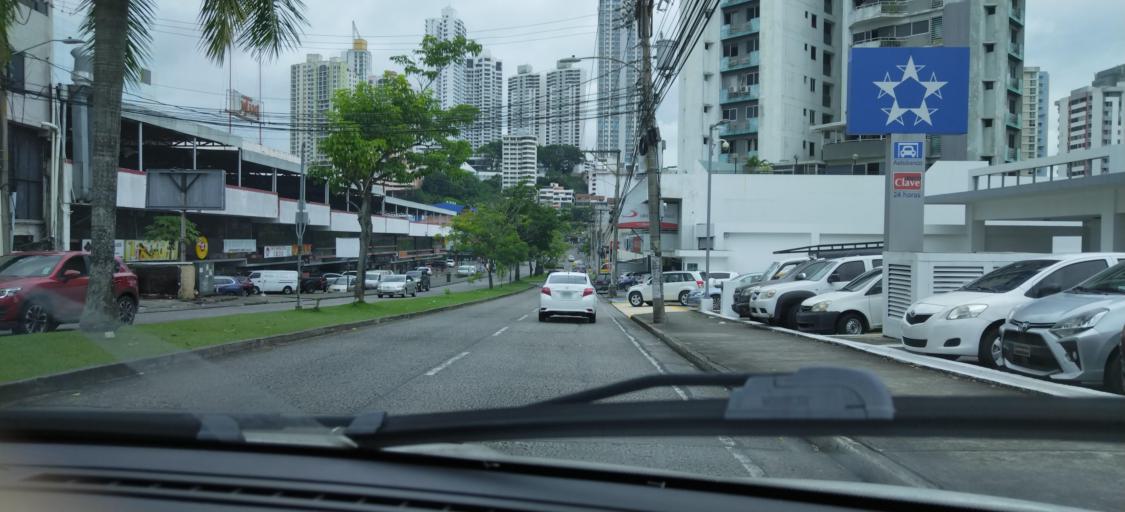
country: PA
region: Panama
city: Panama
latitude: 9.0089
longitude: -79.5367
